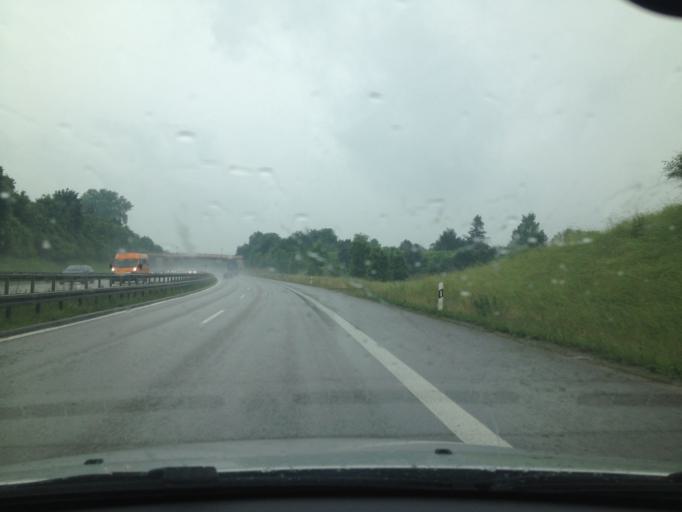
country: DE
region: Bavaria
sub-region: Swabia
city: Klosterlechfeld
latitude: 48.1589
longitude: 10.8401
